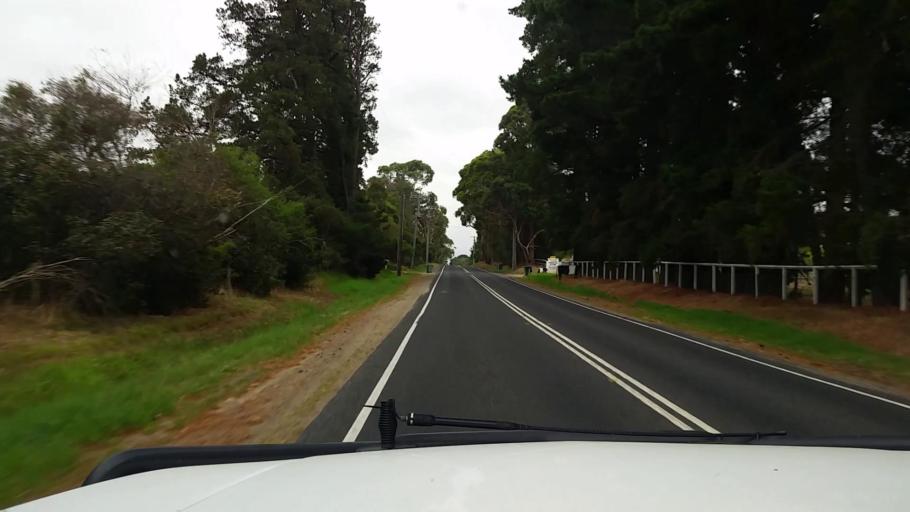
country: AU
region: Victoria
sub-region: Mornington Peninsula
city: Hastings
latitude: -38.2817
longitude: 145.1456
